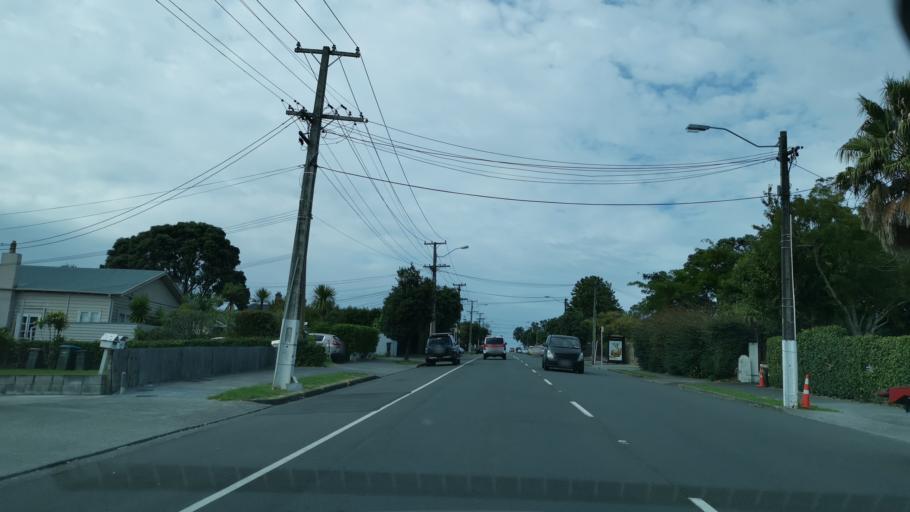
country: NZ
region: Auckland
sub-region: Auckland
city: Rosebank
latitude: -36.8883
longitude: 174.7006
